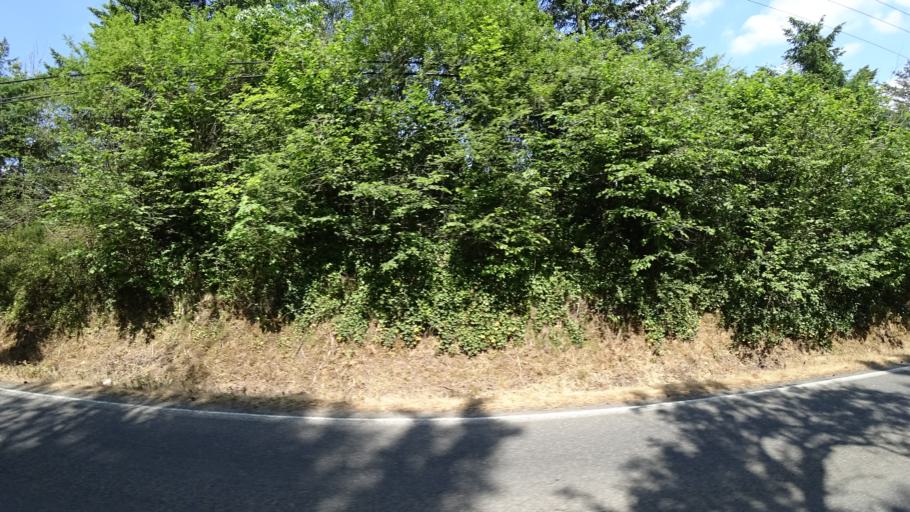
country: US
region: Oregon
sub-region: Clackamas County
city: Happy Valley
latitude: 45.4613
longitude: -122.5093
